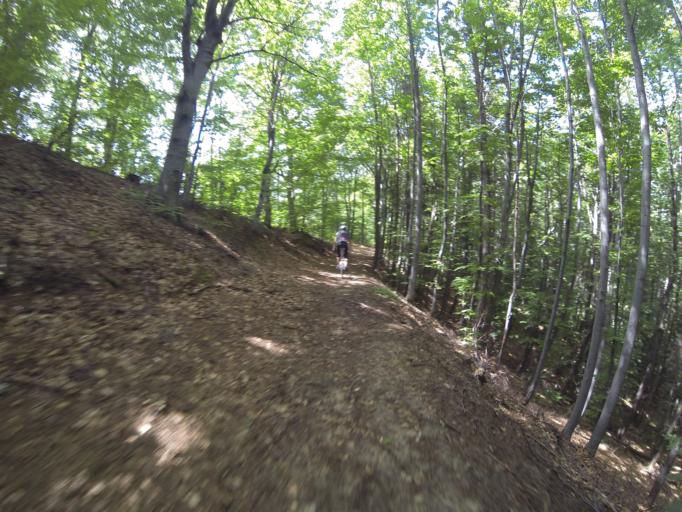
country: RO
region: Valcea
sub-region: Oras Baile Olanesti
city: Baile Olanesti
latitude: 45.2185
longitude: 24.1985
